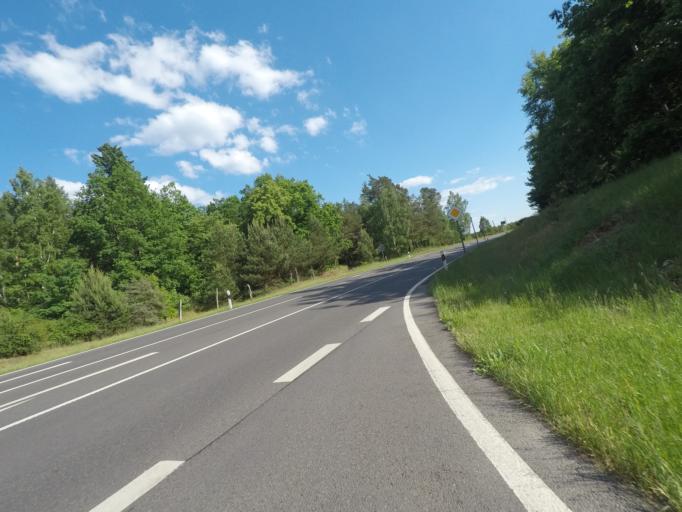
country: DE
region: Brandenburg
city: Eberswalde
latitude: 52.8580
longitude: 13.7965
